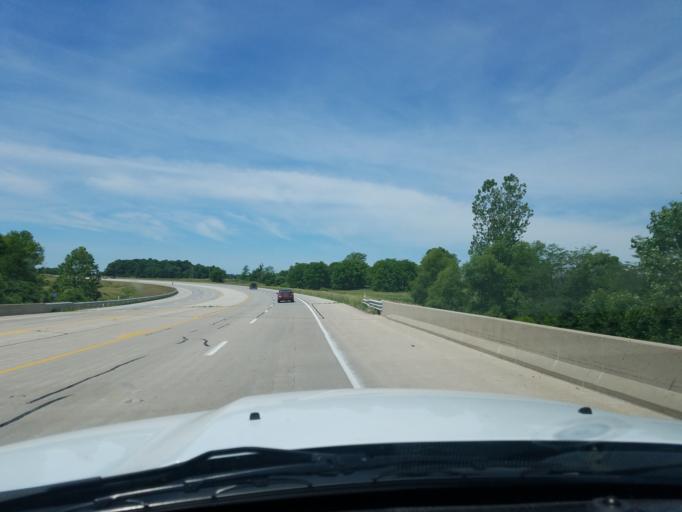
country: US
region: Indiana
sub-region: Delaware County
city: Yorktown
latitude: 40.1209
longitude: -85.4713
